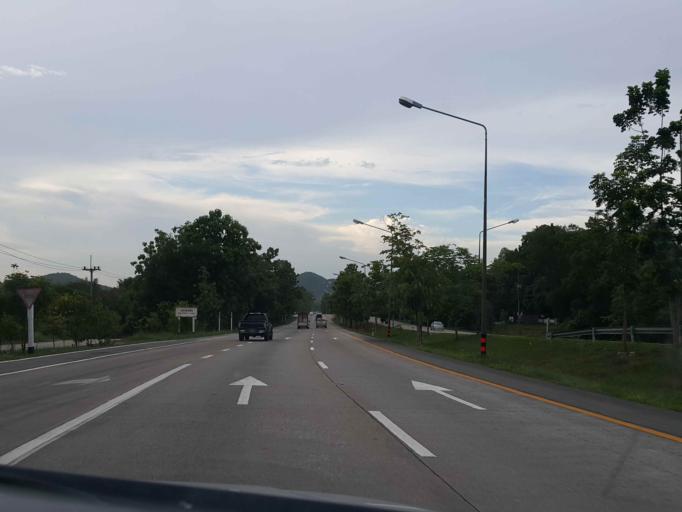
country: TH
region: Lamphun
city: Mae Tha
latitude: 18.4662
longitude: 99.1277
